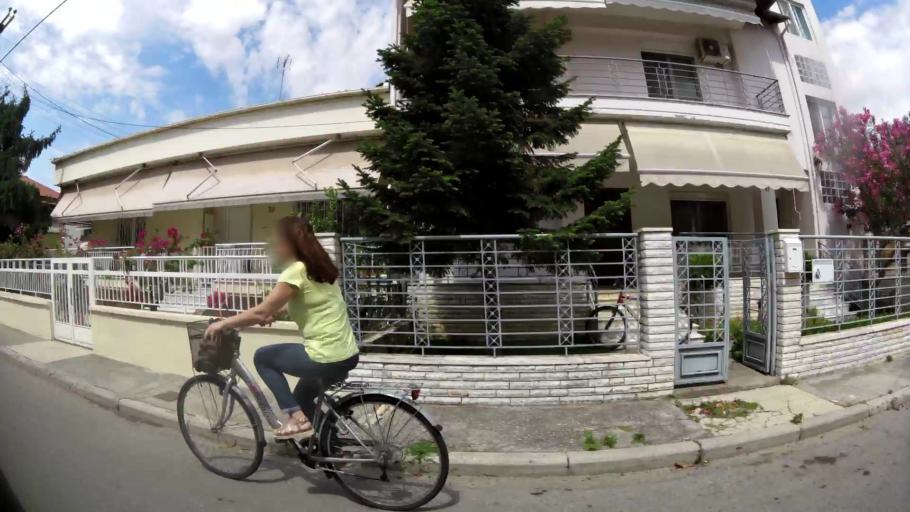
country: GR
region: Central Macedonia
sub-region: Nomos Pierias
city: Katerini
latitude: 40.2769
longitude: 22.5001
